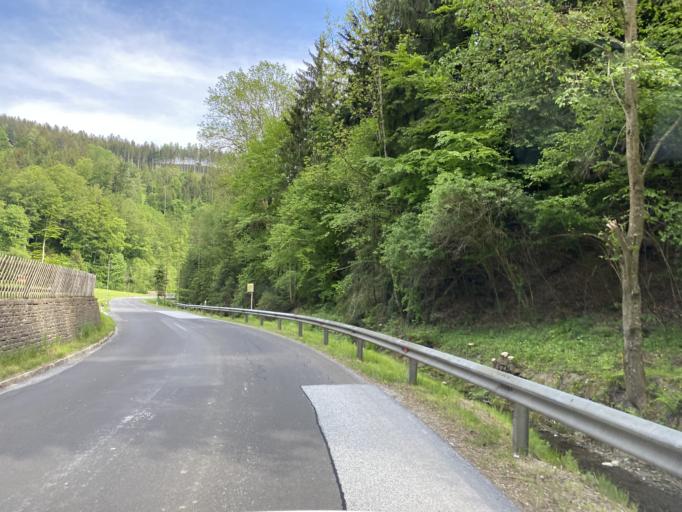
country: AT
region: Styria
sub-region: Politischer Bezirk Weiz
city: Koglhof
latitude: 47.3041
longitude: 15.6695
